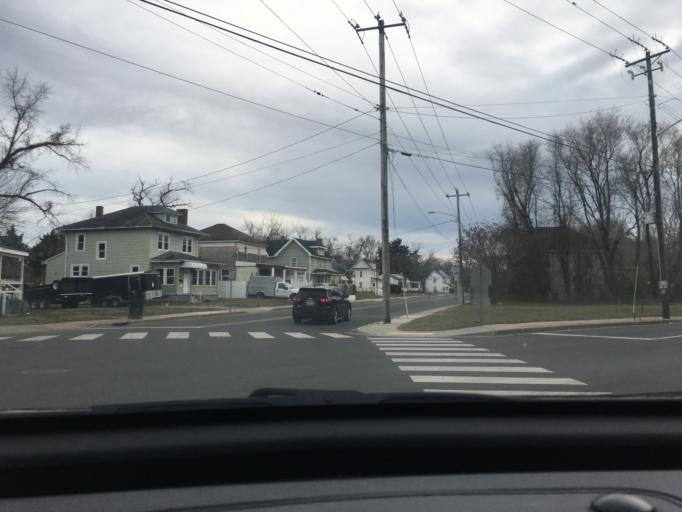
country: US
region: Maryland
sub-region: Wicomico County
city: Salisbury
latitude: 38.3715
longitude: -75.6072
